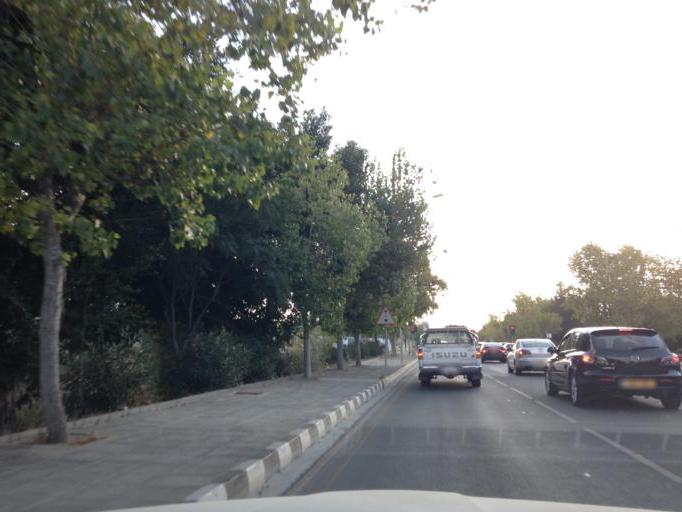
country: CY
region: Pafos
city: Paphos
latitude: 34.7620
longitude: 32.4385
